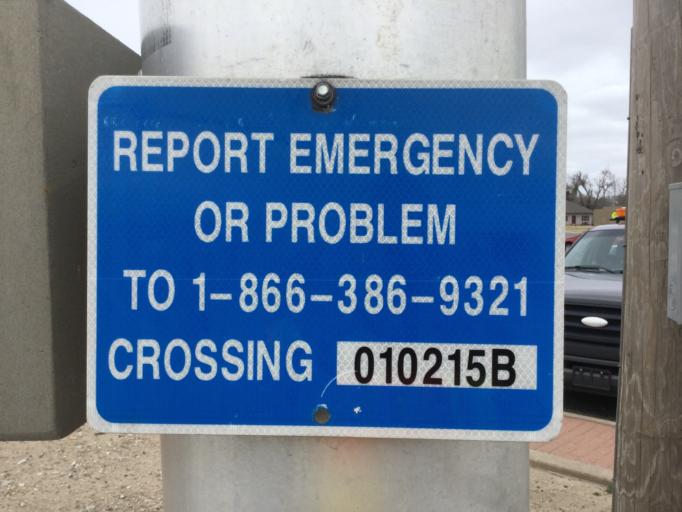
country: US
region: Kansas
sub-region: Barton County
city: Great Bend
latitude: 38.3619
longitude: -98.7839
